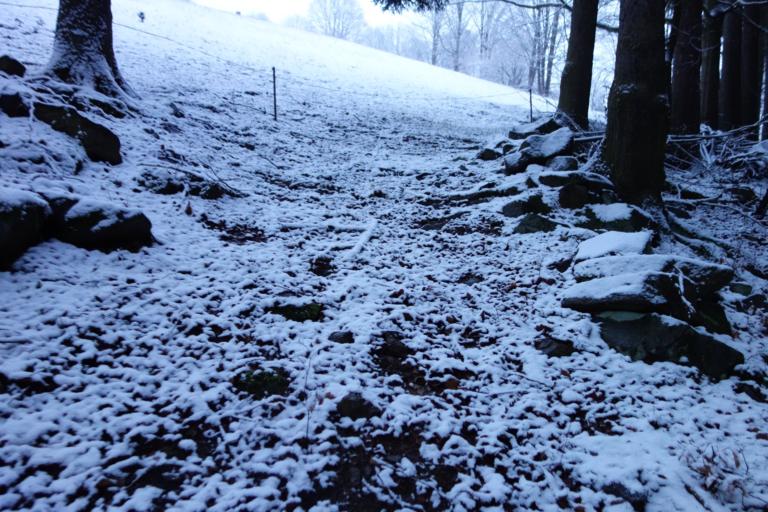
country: DE
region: Saxony
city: Grunhainichen
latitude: 50.7561
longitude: 13.1620
